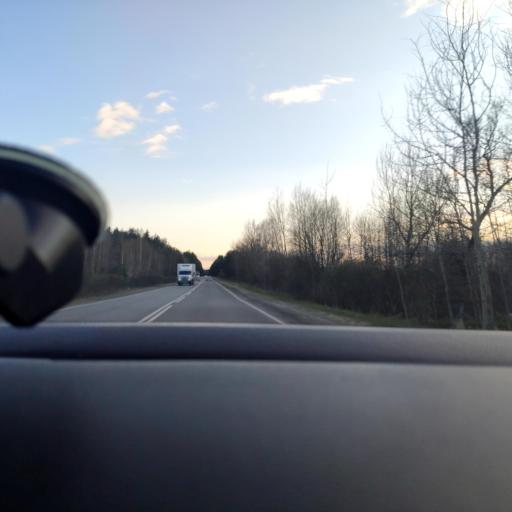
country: RU
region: Moskovskaya
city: Krasnyy Tkach
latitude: 55.4212
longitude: 39.1846
